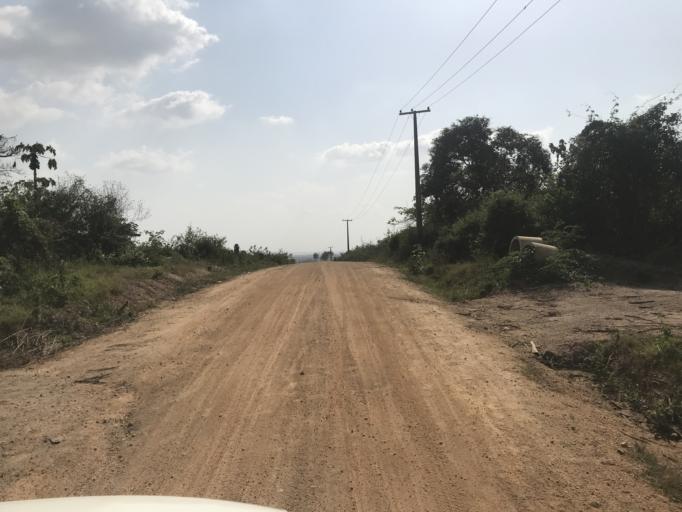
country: NG
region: Osun
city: Osogbo
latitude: 7.8485
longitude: 4.5824
